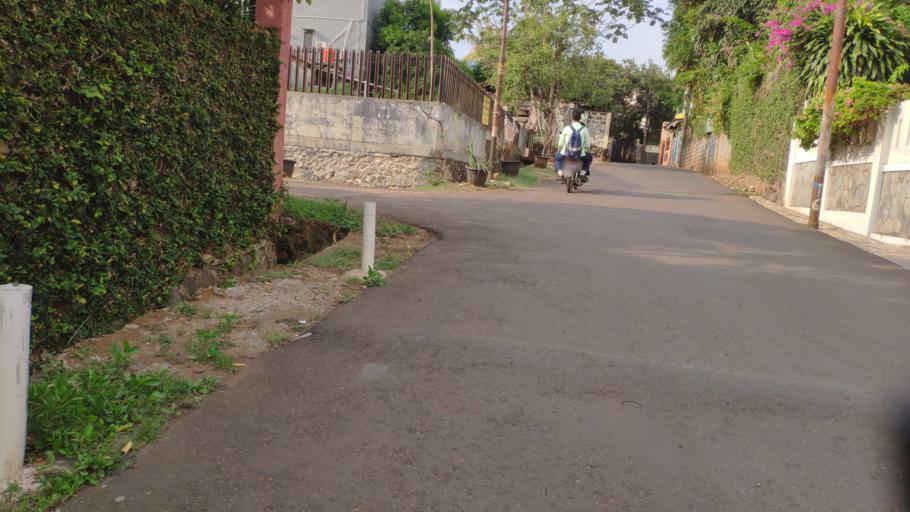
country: ID
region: West Java
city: Pamulang
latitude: -6.2979
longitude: 106.8035
